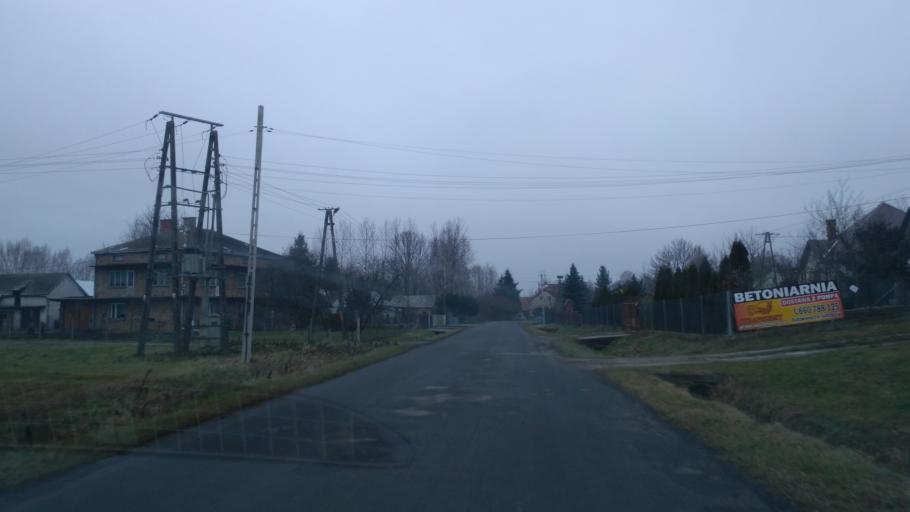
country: PL
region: Subcarpathian Voivodeship
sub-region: Powiat przeworski
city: Zarzecze
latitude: 49.9555
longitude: 22.5666
